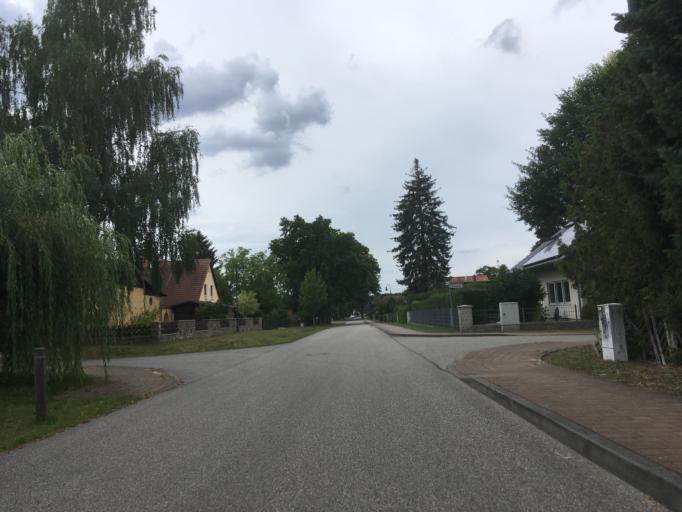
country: DE
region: Berlin
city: Buch
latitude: 52.6545
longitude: 13.5202
